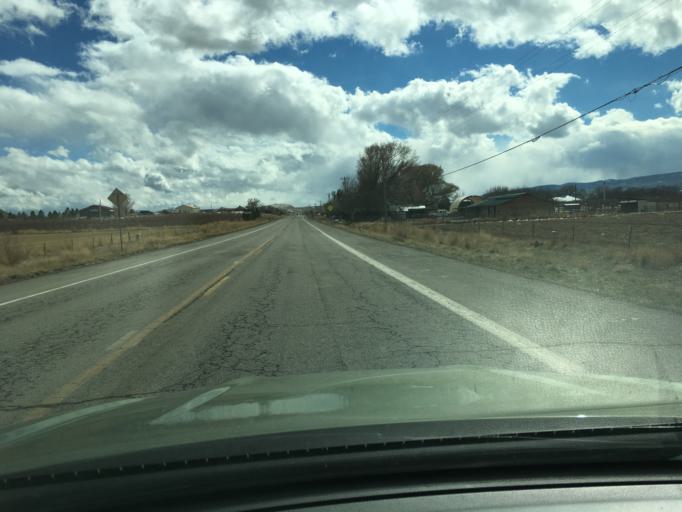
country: US
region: Colorado
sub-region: Mesa County
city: Clifton
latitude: 39.0394
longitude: -108.4595
